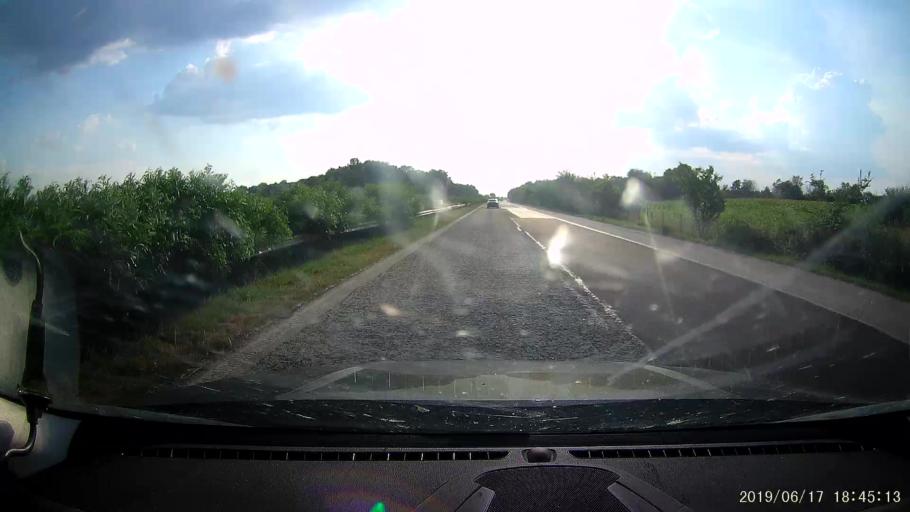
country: BG
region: Plovdiv
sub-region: Obshtina Brezovo
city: Brezovo
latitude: 42.1940
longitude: 25.1573
